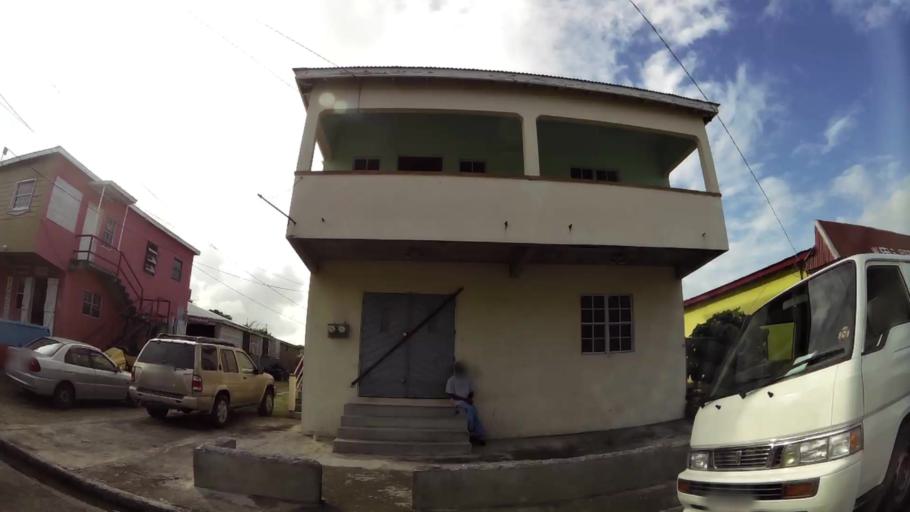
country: AG
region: Saint John
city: Saint John's
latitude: 17.1258
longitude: -61.8279
